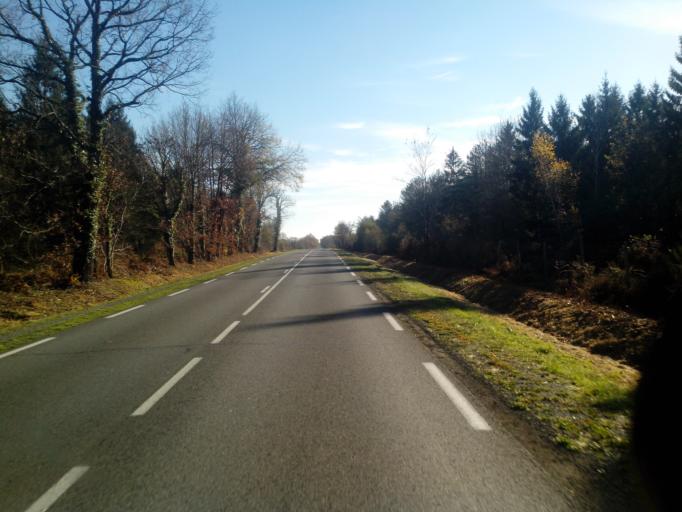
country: FR
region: Limousin
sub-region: Departement de la Haute-Vienne
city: Bussiere-Poitevine
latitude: 46.2534
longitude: 0.8796
